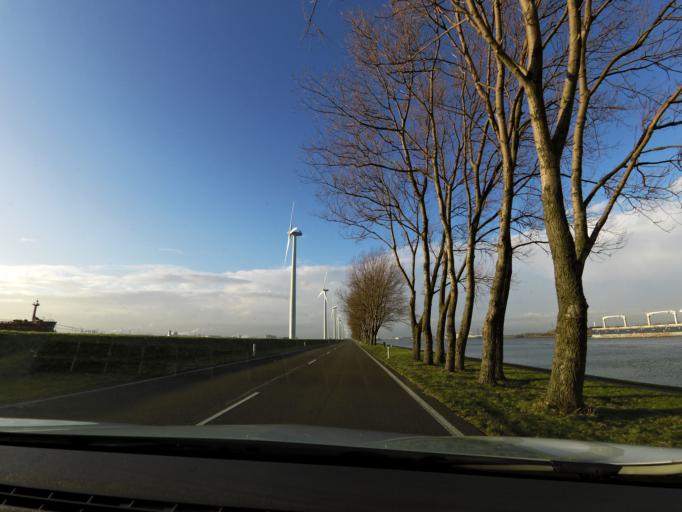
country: NL
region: South Holland
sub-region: Gemeente Westland
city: Maasdijk
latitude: 51.9419
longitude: 4.1815
